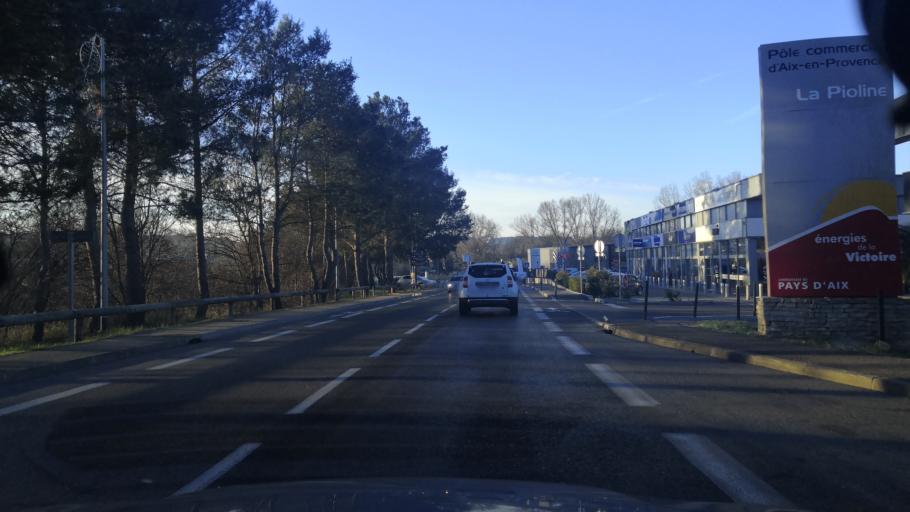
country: FR
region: Provence-Alpes-Cote d'Azur
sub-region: Departement des Bouches-du-Rhone
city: Aix-en-Provence
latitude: 43.5105
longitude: 5.4096
